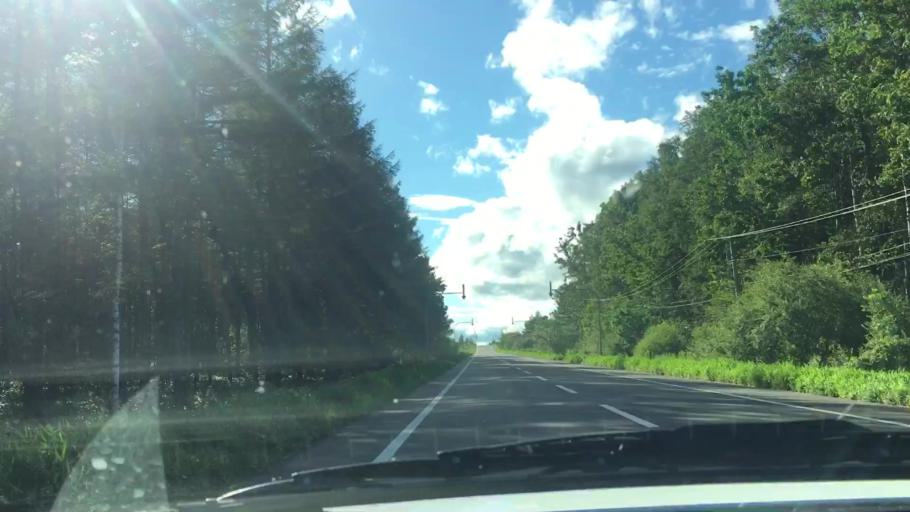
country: JP
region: Hokkaido
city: Otofuke
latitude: 43.1634
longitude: 143.1483
